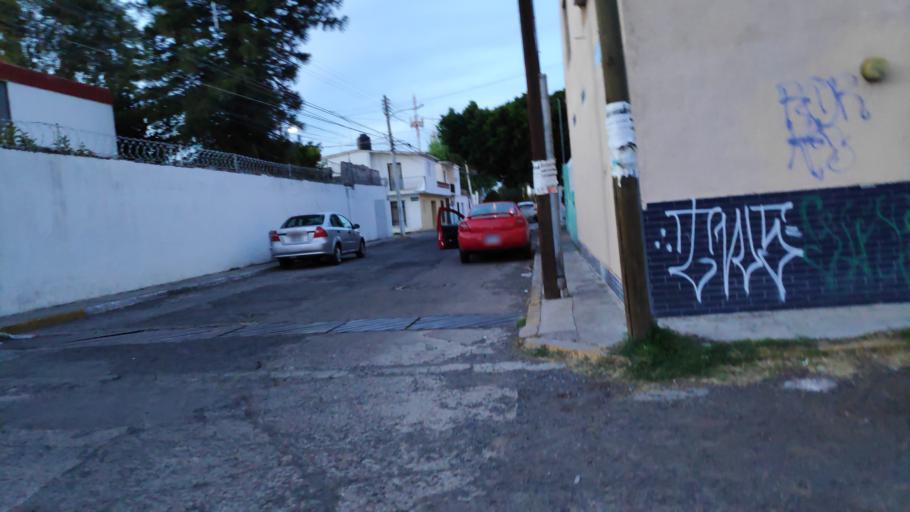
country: MX
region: Queretaro
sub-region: Queretaro
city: Santiago de Queretaro
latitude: 20.5839
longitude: -100.3830
